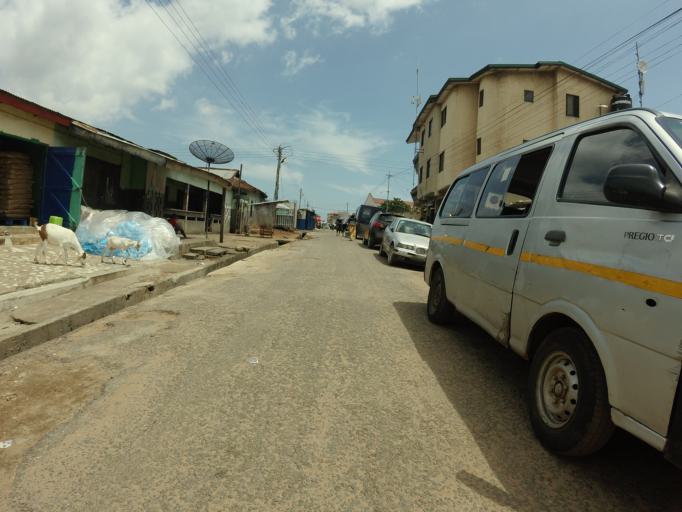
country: GH
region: Greater Accra
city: Accra
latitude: 5.5828
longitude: -0.2011
